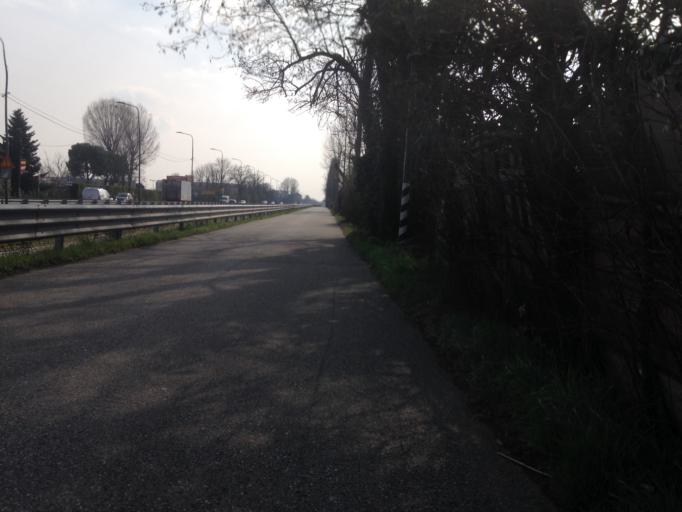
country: IT
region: Lombardy
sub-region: Citta metropolitana di Milano
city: Rozzano
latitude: 45.4213
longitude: 9.1666
